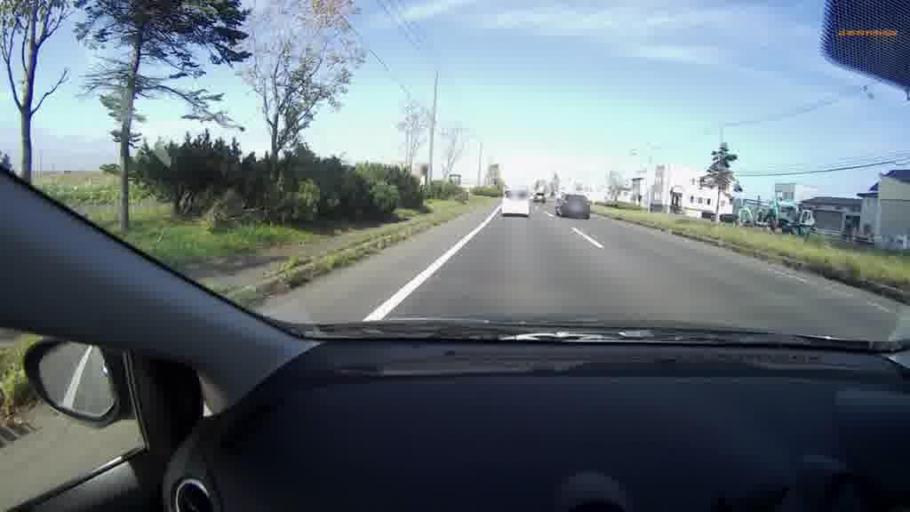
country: JP
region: Hokkaido
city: Kushiro
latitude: 43.0053
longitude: 144.4163
